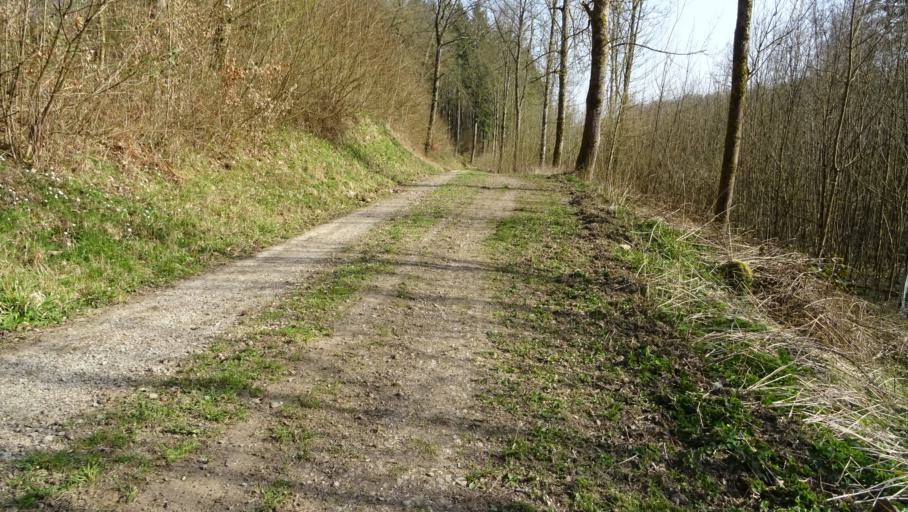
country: DE
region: Baden-Wuerttemberg
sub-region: Regierungsbezirk Stuttgart
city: Roigheim
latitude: 49.3823
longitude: 9.3462
